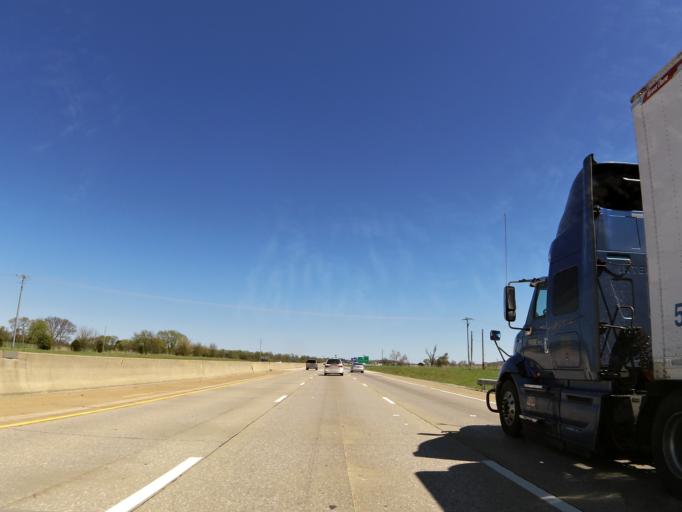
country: US
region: Kentucky
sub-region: Edmonson County
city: Brownsville
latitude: 37.0391
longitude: -86.2270
